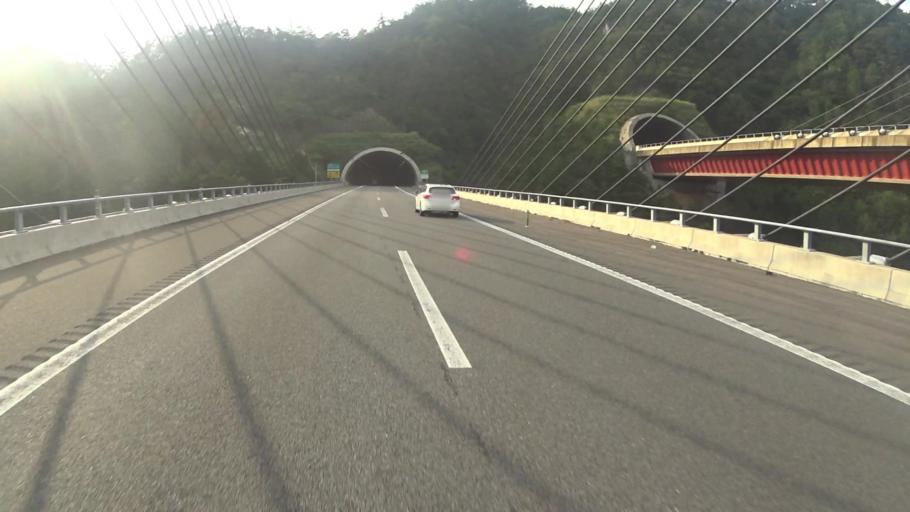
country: JP
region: Shiga Prefecture
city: Kusatsu
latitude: 34.9410
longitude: 136.0322
